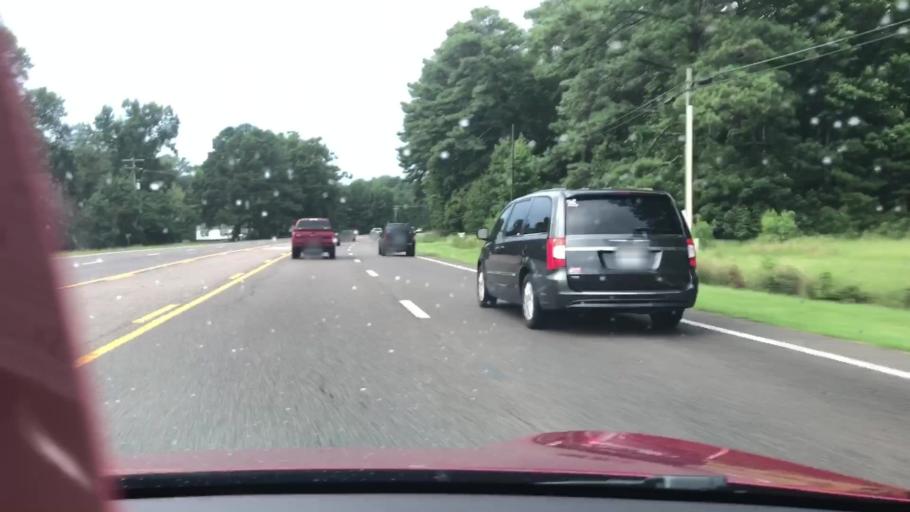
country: US
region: North Carolina
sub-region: Currituck County
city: Currituck
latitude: 36.2849
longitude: -75.9195
